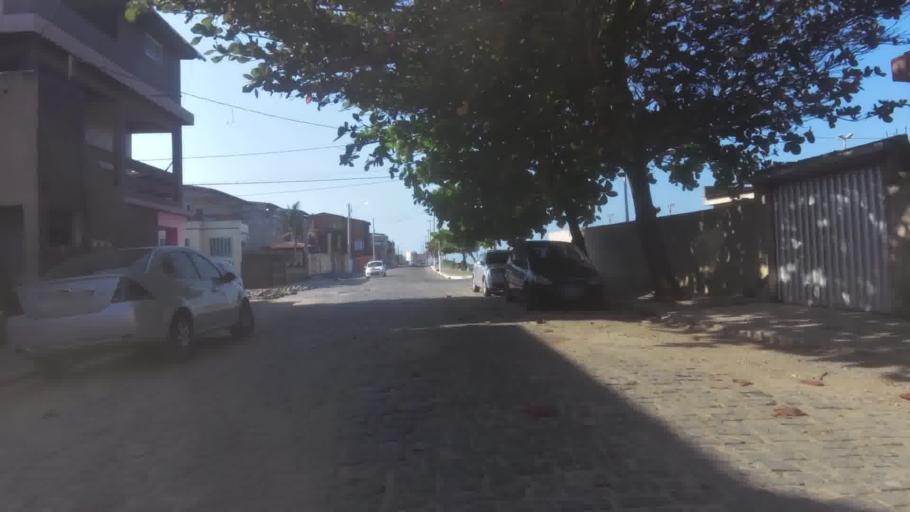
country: BR
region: Espirito Santo
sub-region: Itapemirim
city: Itapemirim
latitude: -21.0133
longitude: -40.8098
